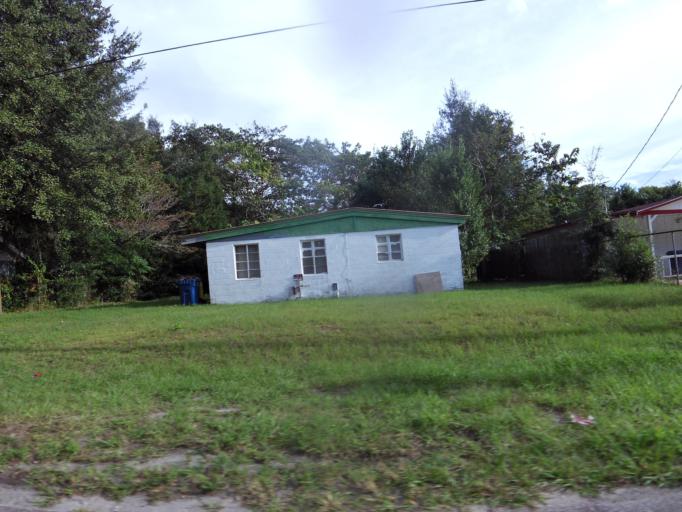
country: US
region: Florida
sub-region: Duval County
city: Jacksonville
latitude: 30.4271
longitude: -81.6720
